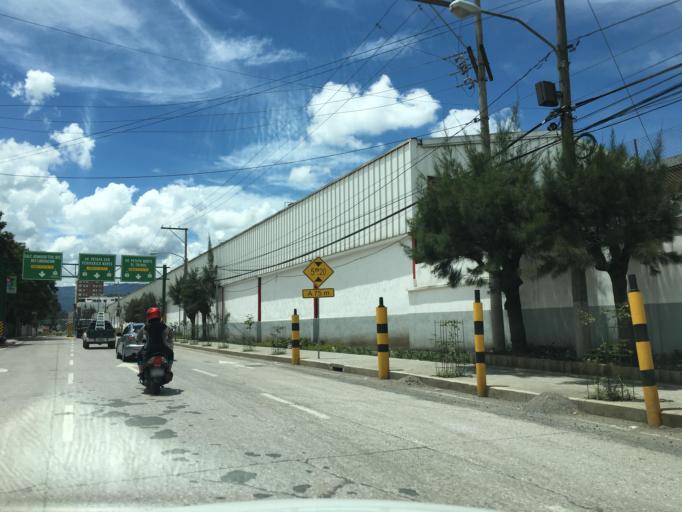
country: GT
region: Guatemala
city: Santa Catarina Pinula
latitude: 14.5889
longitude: -90.5398
